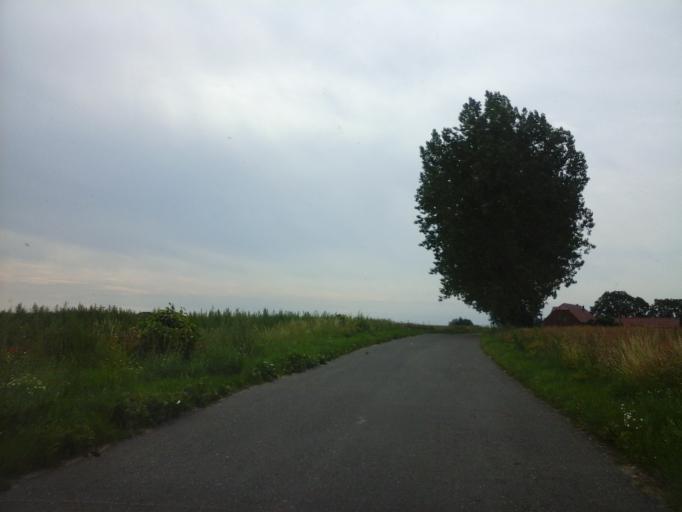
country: PL
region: West Pomeranian Voivodeship
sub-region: Powiat choszczenski
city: Recz
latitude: 53.2094
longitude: 15.5501
